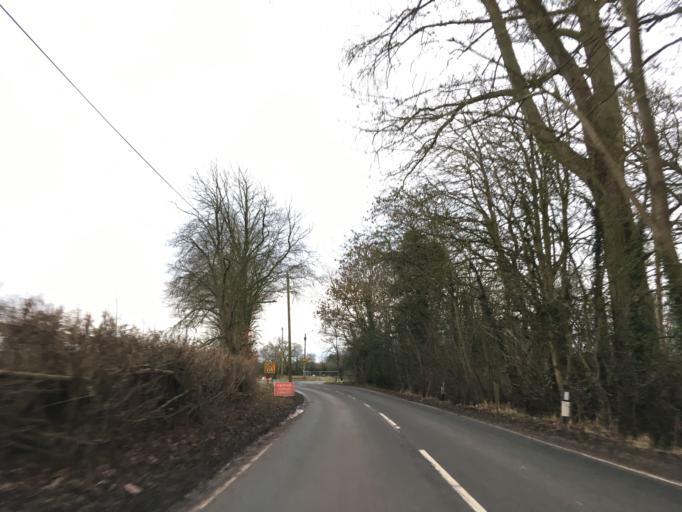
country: GB
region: England
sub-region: South Gloucestershire
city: Winterbourne
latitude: 51.5360
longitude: -2.5237
